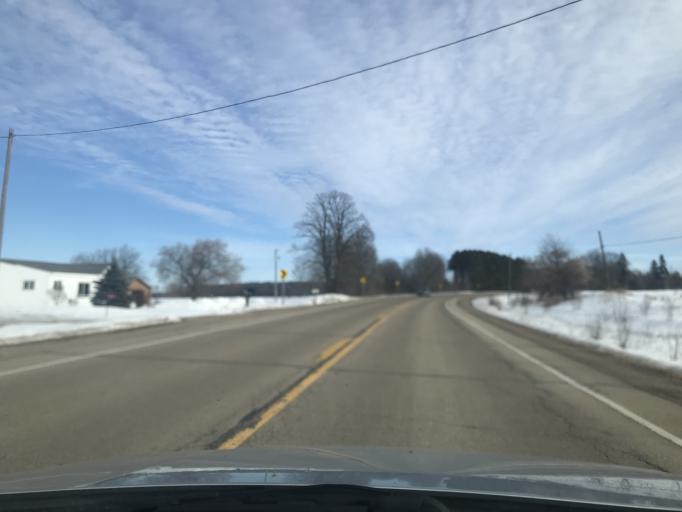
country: US
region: Wisconsin
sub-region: Oconto County
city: Gillett
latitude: 44.8855
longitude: -88.3329
